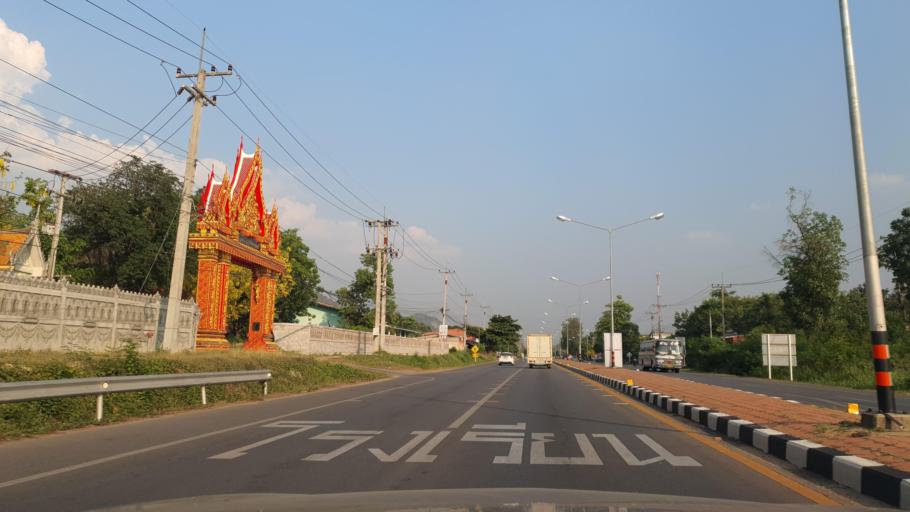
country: TH
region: Kanchanaburi
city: Kanchanaburi
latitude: 14.0787
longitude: 99.4760
